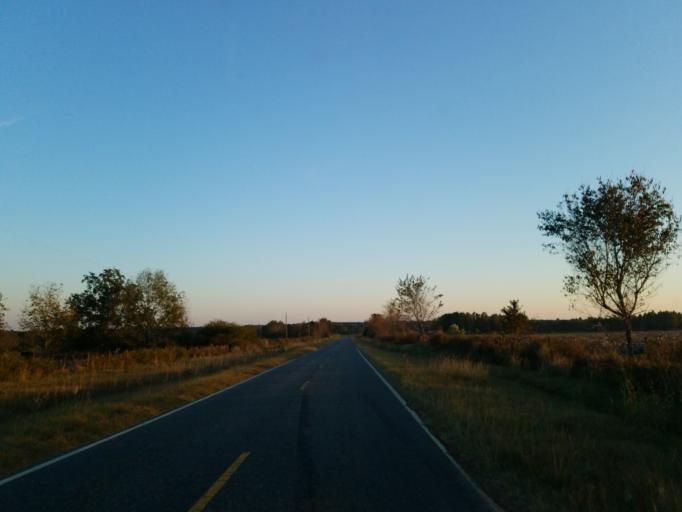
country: US
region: Georgia
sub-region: Ben Hill County
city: Fitzgerald
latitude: 31.6934
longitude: -83.4133
